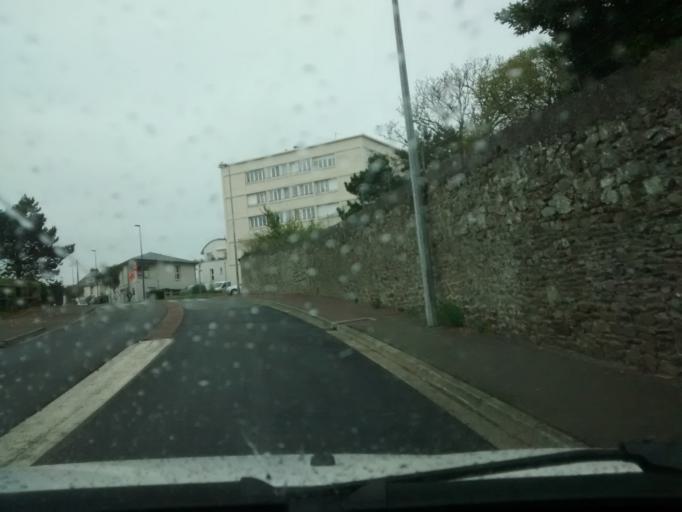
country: FR
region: Lower Normandy
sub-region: Departement de la Manche
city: Granville
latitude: 48.8325
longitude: -1.5849
